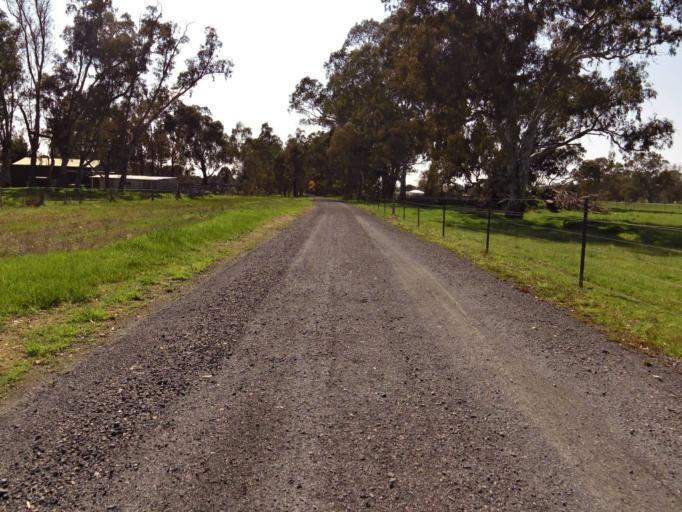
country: AU
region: Victoria
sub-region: Murrindindi
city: Alexandra
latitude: -37.1097
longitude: 145.6125
